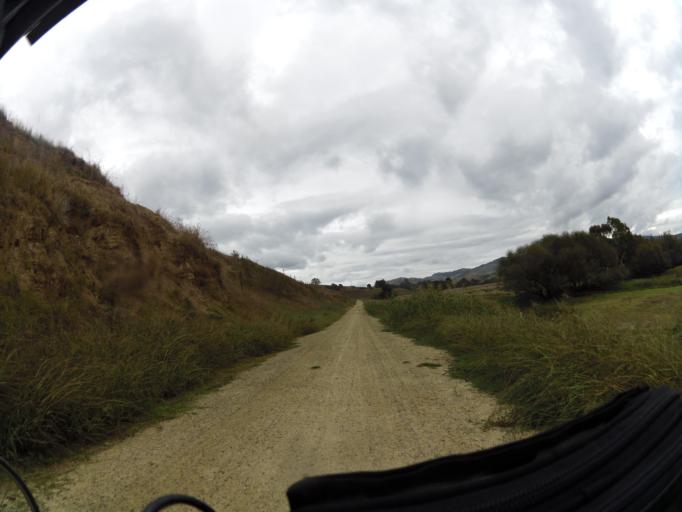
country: AU
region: New South Wales
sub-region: Albury Municipality
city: East Albury
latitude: -36.1920
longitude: 147.2980
